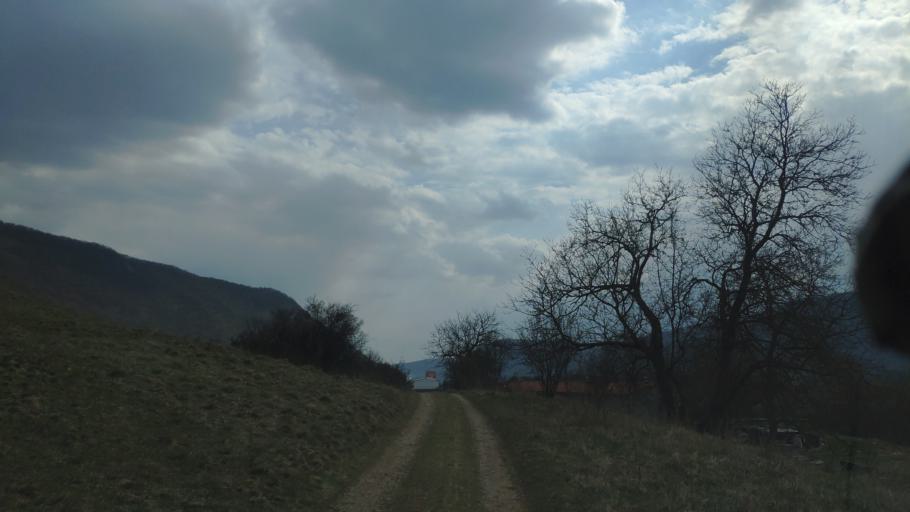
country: SK
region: Kosicky
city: Roznava
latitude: 48.6146
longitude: 20.3882
